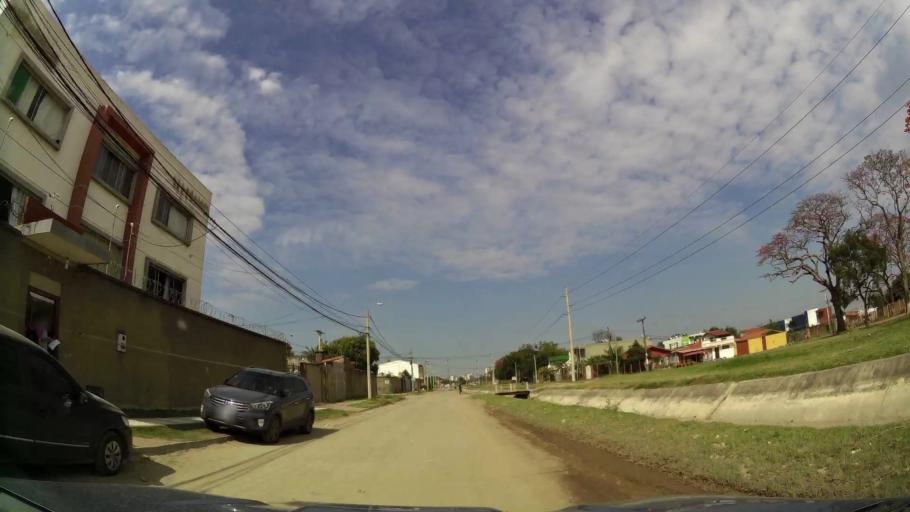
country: BO
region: Santa Cruz
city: Santa Cruz de la Sierra
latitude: -17.7262
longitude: -63.1747
